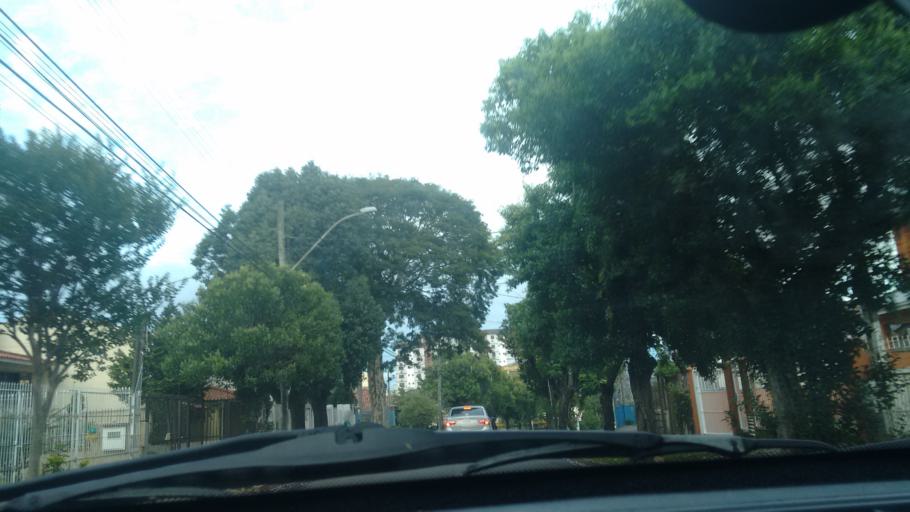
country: BR
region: Rio Grande do Sul
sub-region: Porto Alegre
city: Porto Alegre
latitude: -30.0087
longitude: -51.1606
